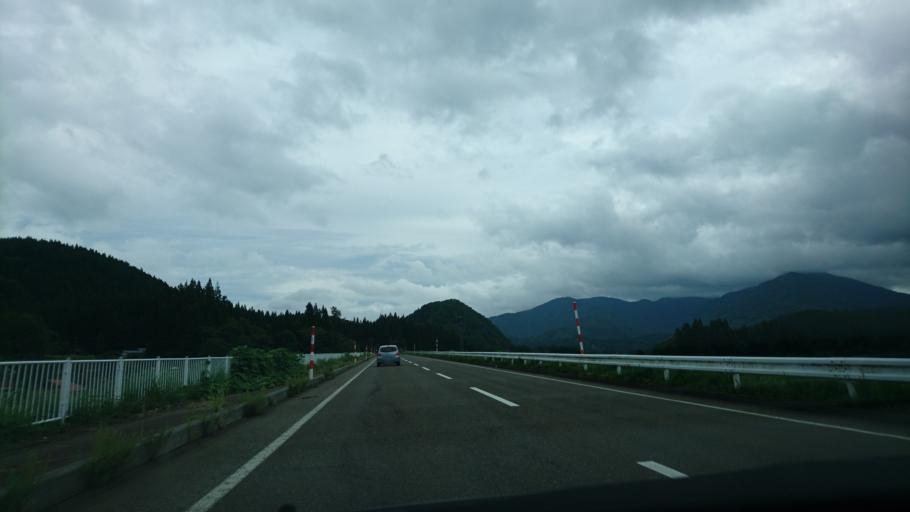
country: JP
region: Akita
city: Yuzawa
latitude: 38.9849
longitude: 140.4846
